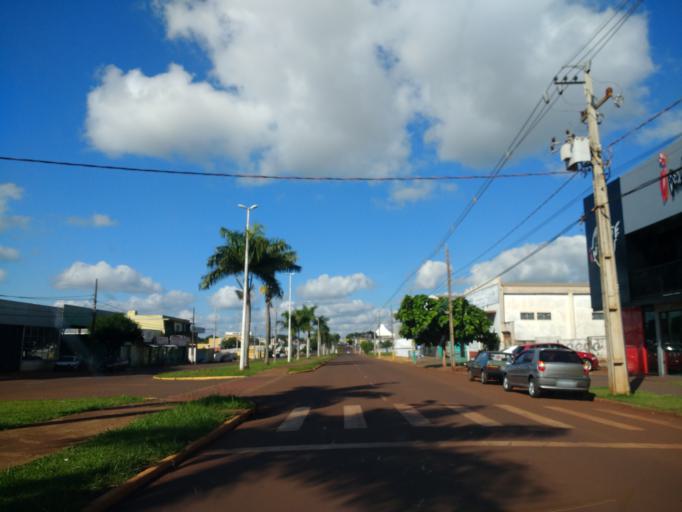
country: BR
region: Parana
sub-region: Palotina
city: Palotina
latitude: -24.4096
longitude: -53.5295
